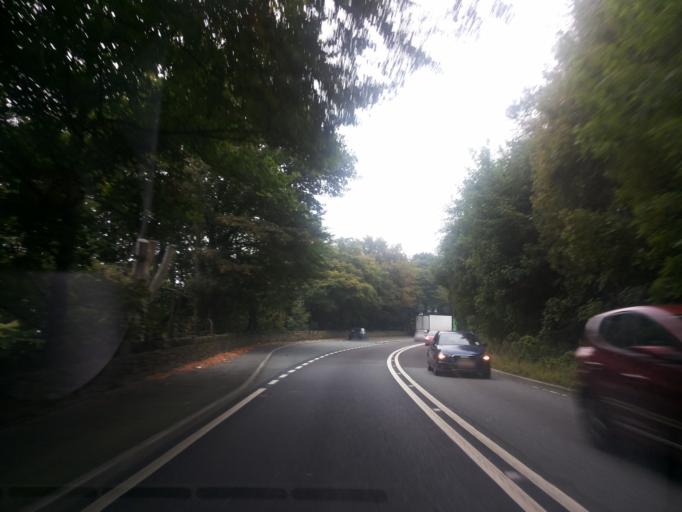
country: GB
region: England
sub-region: Derbyshire
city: Glossop
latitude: 53.4793
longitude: -1.9481
